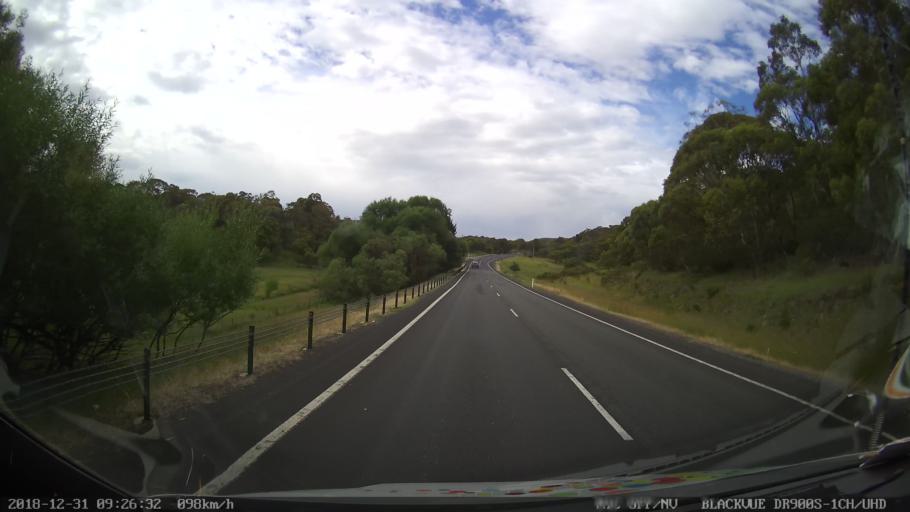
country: AU
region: New South Wales
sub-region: Snowy River
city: Jindabyne
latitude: -36.4488
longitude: 148.4946
